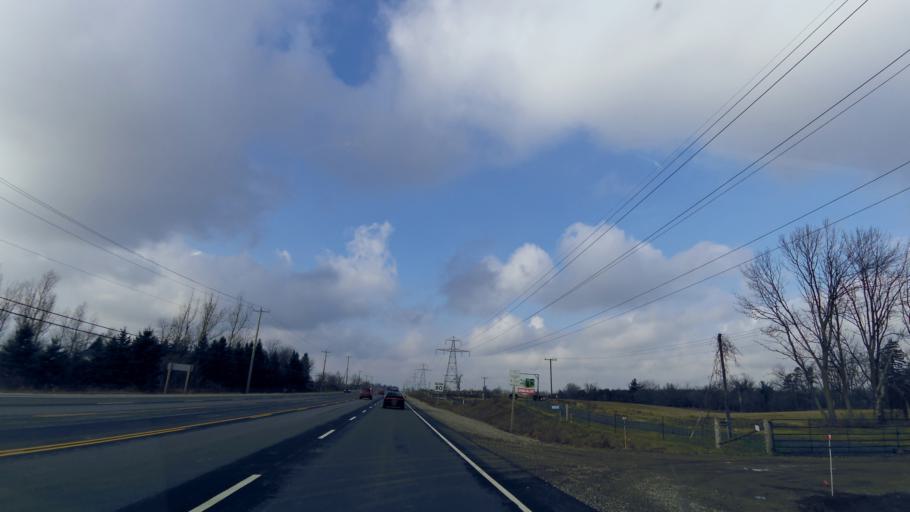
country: CA
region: Ontario
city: Ancaster
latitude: 43.3890
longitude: -80.0219
